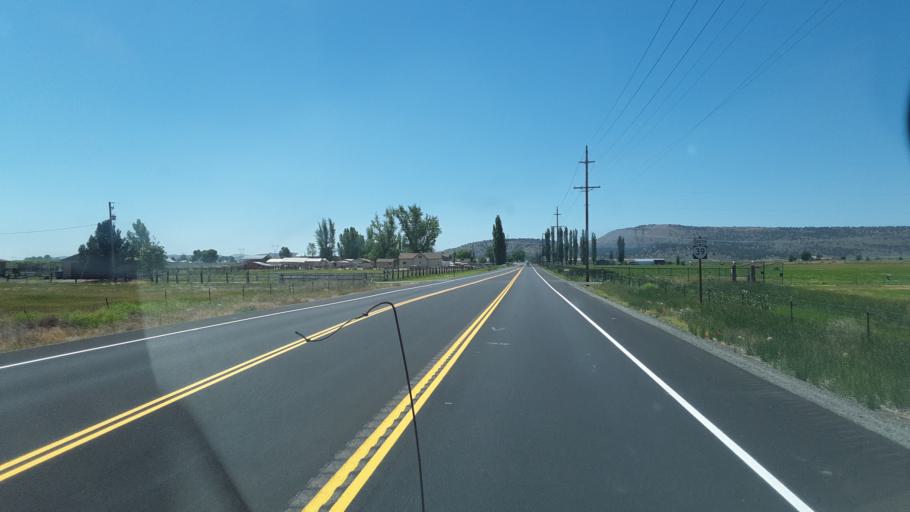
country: US
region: Oregon
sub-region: Klamath County
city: Altamont
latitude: 42.1108
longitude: -121.6986
